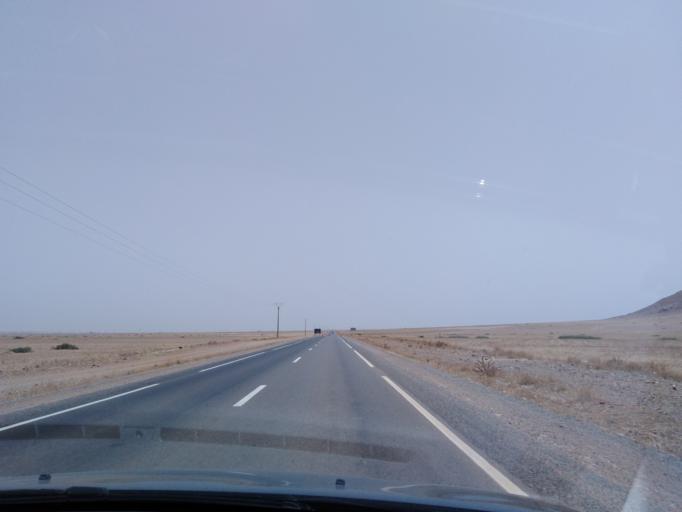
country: MA
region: Marrakech-Tensift-Al Haouz
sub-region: Kelaa-Des-Sraghna
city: Sidi Bou Othmane
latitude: 31.9612
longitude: -8.2533
